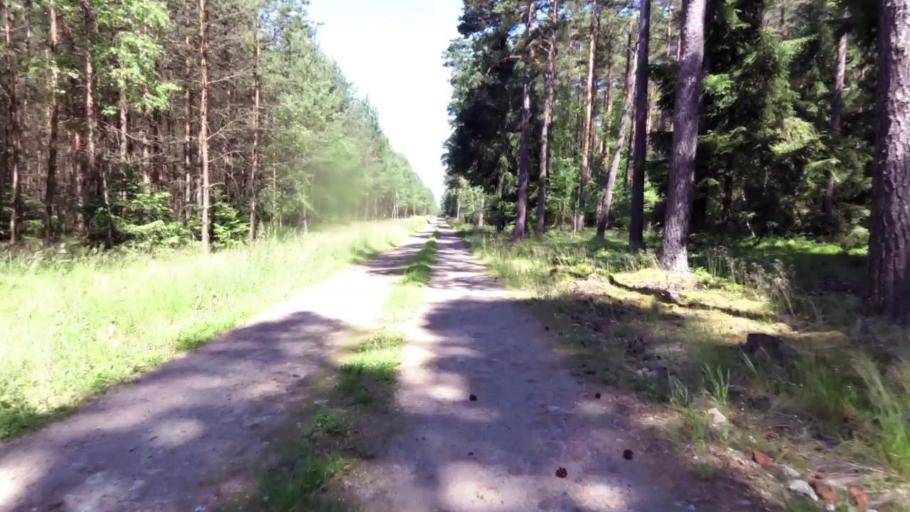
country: PL
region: West Pomeranian Voivodeship
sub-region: Powiat bialogardzki
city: Tychowo
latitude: 53.9172
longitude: 16.1230
